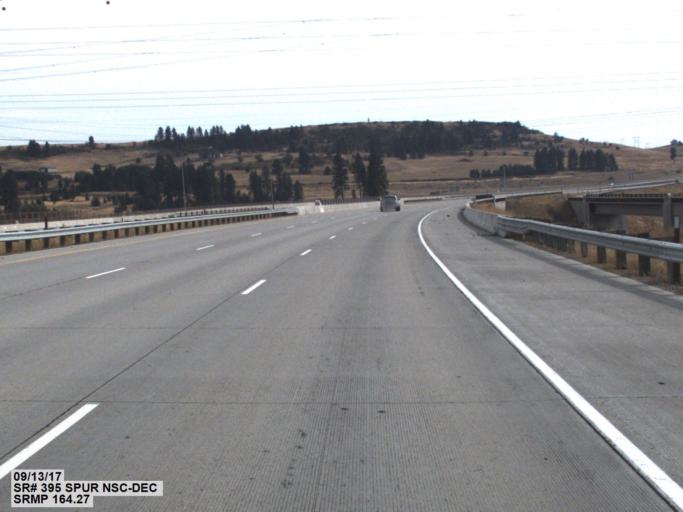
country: US
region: Washington
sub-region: Spokane County
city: Mead
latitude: 47.7536
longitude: -117.3606
